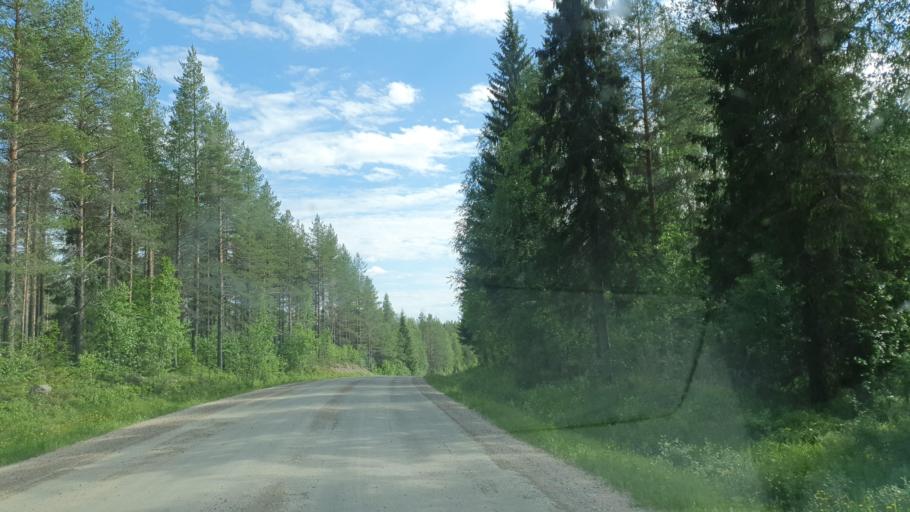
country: FI
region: Kainuu
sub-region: Kehys-Kainuu
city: Kuhmo
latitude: 64.4686
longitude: 29.5382
